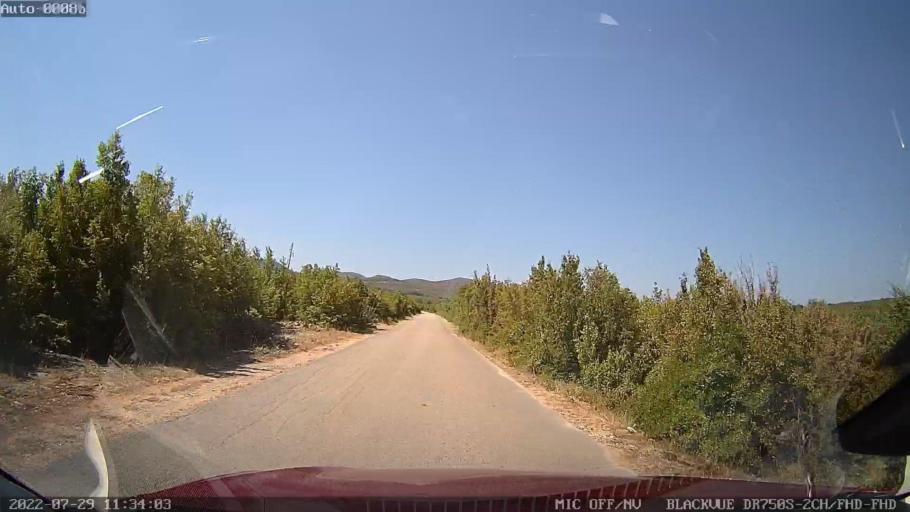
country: HR
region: Zadarska
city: Obrovac
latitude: 44.1812
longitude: 15.7299
